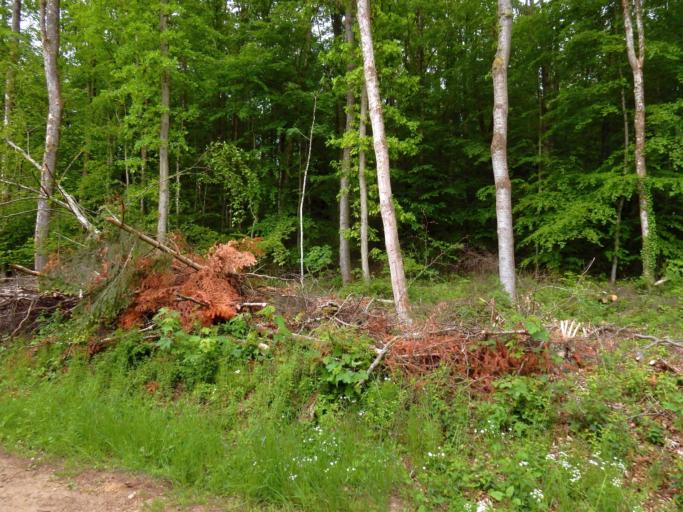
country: LU
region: Diekirch
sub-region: Canton de Diekirch
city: Diekirch
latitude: 49.8912
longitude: 6.1348
